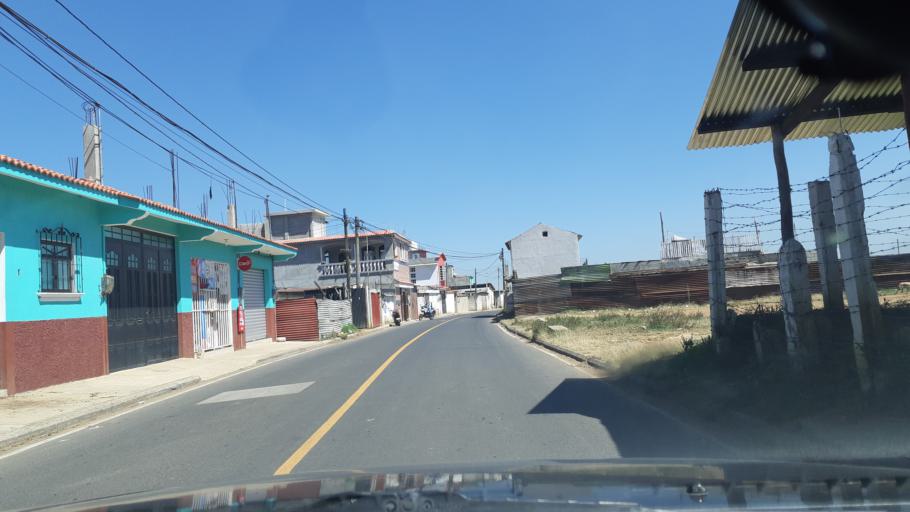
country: GT
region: Chimaltenango
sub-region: Municipio de Zaragoza
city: Zaragoza
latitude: 14.6638
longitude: -90.8637
